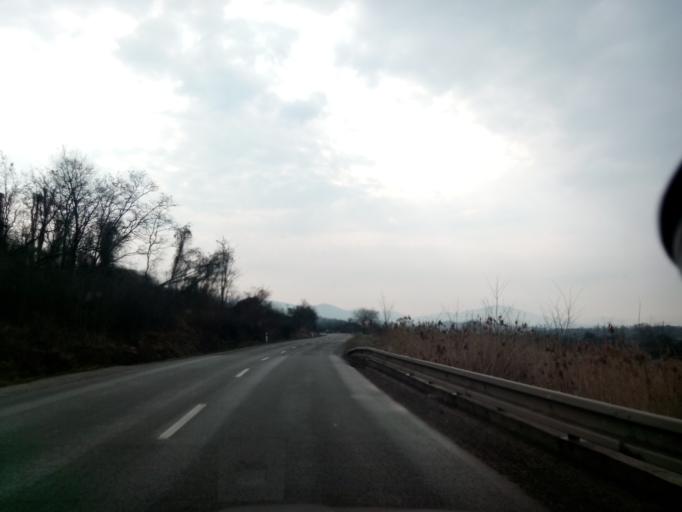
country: SK
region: Kosicky
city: Kosice
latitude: 48.6493
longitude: 21.3622
